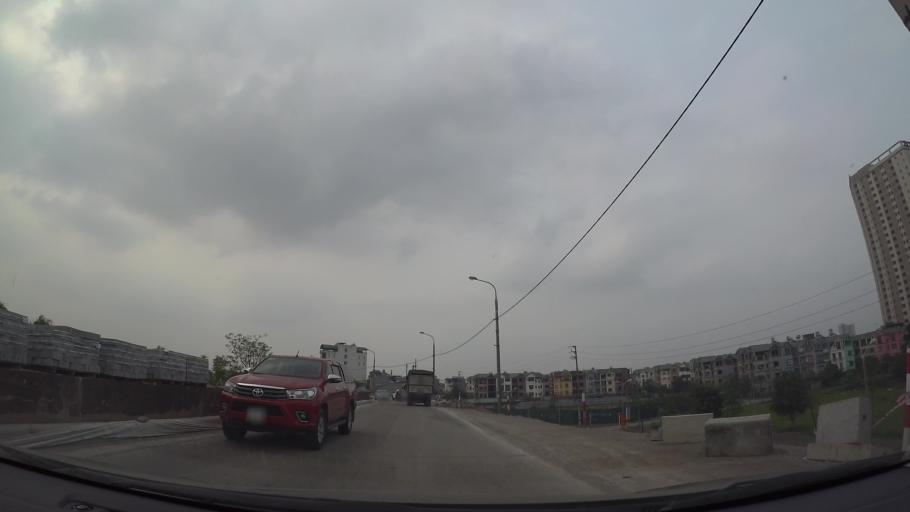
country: VN
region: Ha Noi
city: Trau Quy
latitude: 21.0177
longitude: 105.9043
